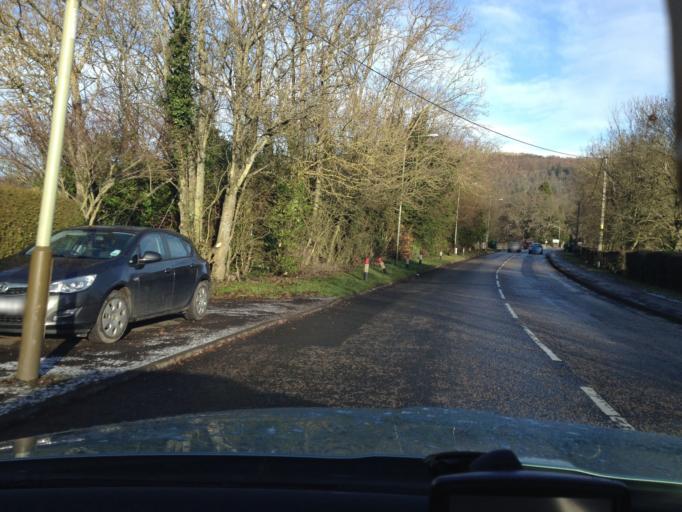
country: GB
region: Scotland
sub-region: Perth and Kinross
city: Bridge of Earn
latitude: 56.3510
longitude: -3.4073
